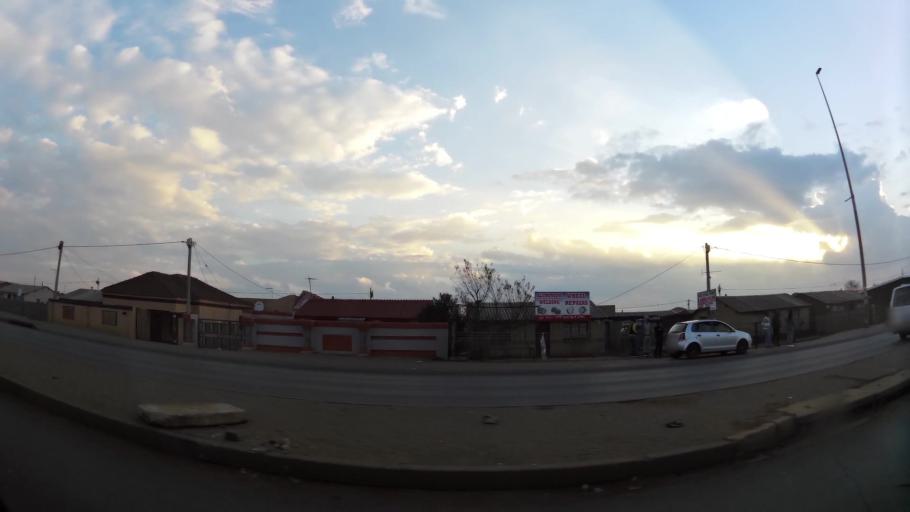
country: ZA
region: Gauteng
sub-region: City of Johannesburg Metropolitan Municipality
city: Orange Farm
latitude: -26.5714
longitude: 27.8379
